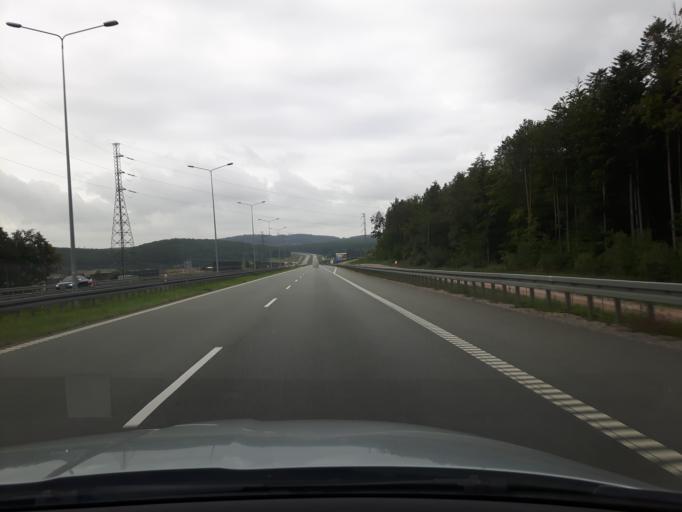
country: PL
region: Swietokrzyskie
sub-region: Powiat kielecki
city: Piekoszow
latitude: 50.8446
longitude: 20.4871
